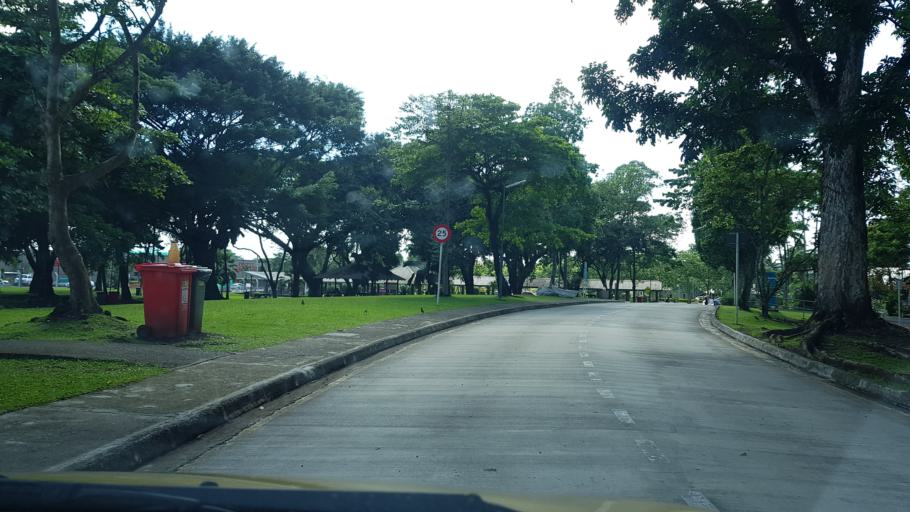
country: FJ
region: Central
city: Suva
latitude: -18.1476
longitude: 178.4455
